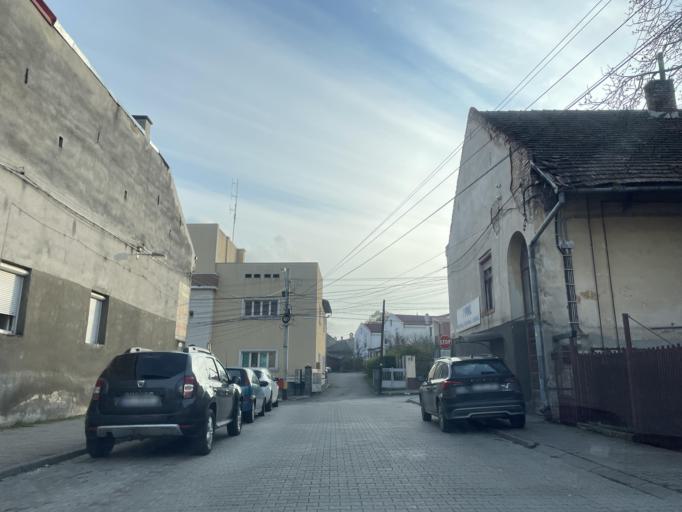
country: RO
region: Mures
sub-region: Municipiul Reghin
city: Reghin
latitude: 46.7818
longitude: 24.6976
